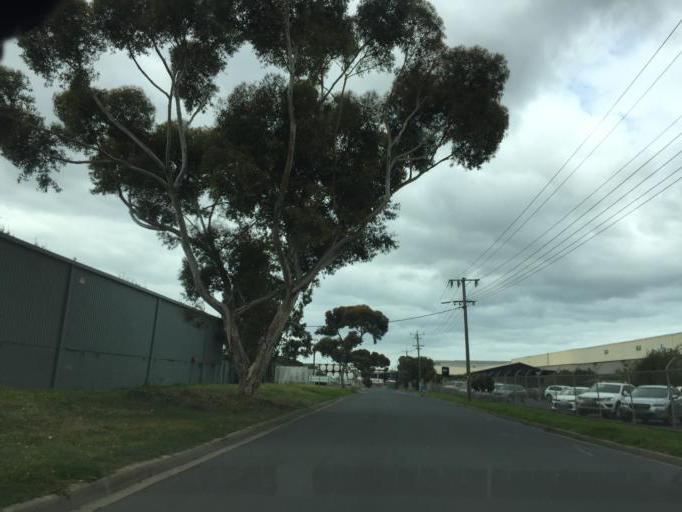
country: AU
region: Victoria
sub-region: Brimbank
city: Brooklyn
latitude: -37.8036
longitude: 144.8495
